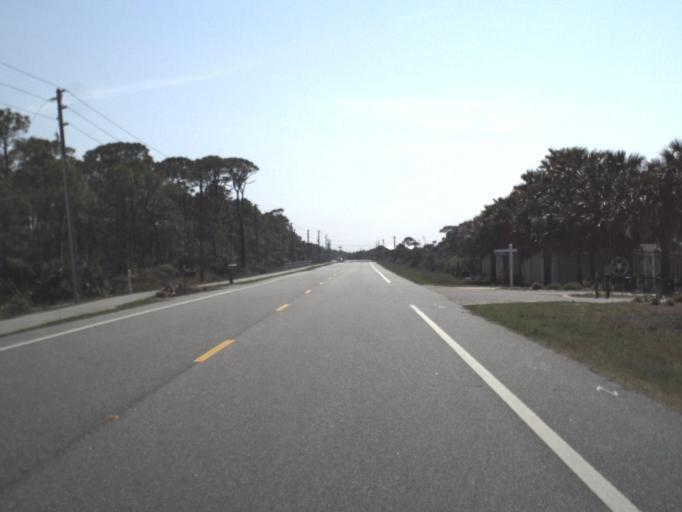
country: US
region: Florida
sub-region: Gulf County
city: Port Saint Joe
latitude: 29.7219
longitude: -85.3868
